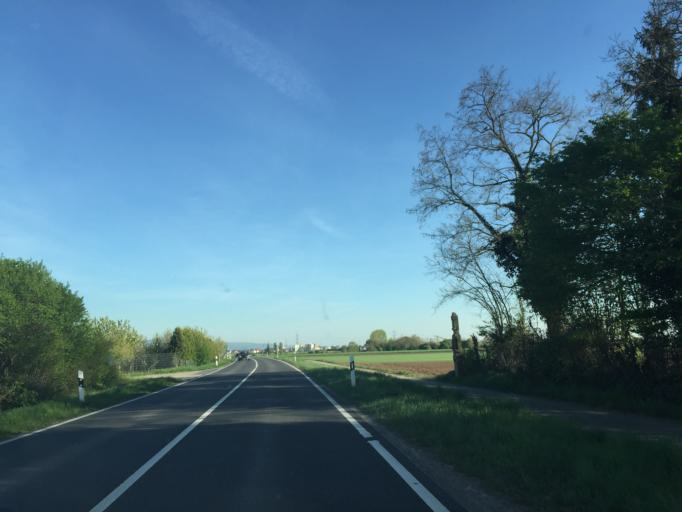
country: DE
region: Hesse
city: Viernheim
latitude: 49.5267
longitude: 8.5837
